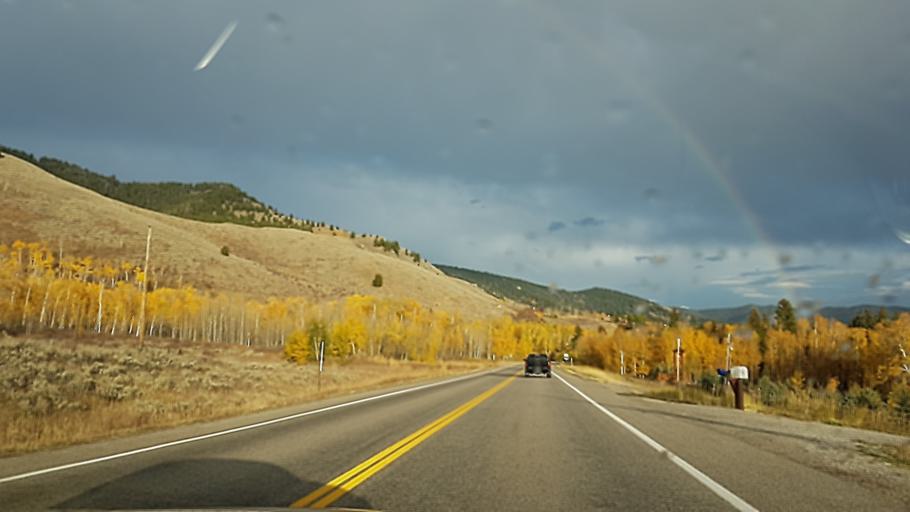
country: US
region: Montana
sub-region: Gallatin County
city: West Yellowstone
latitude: 44.6667
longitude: -111.3918
